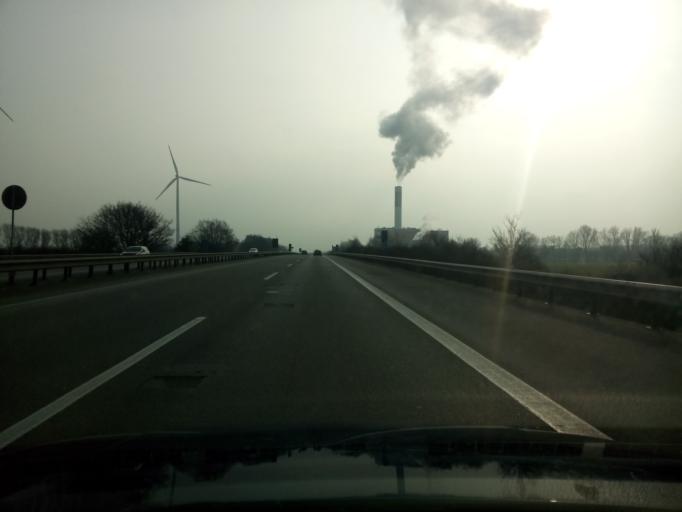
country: DE
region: Lower Saxony
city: Schiffdorf
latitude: 53.5538
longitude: 8.6195
